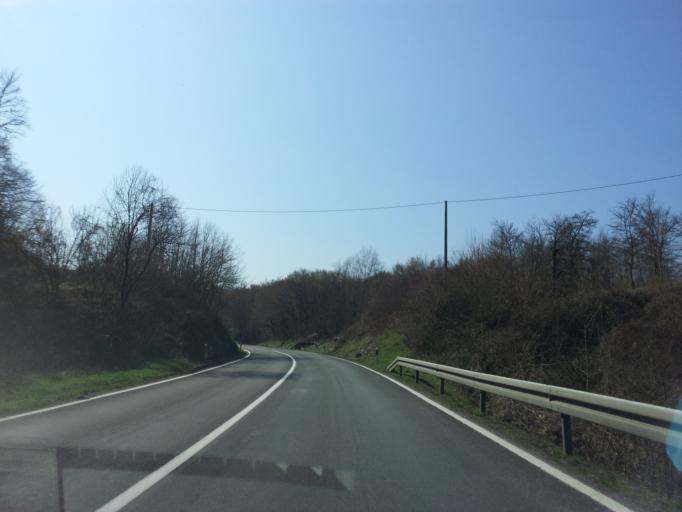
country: HR
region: Karlovacka
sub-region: Grad Karlovac
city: Slunj
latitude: 45.1827
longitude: 15.5607
